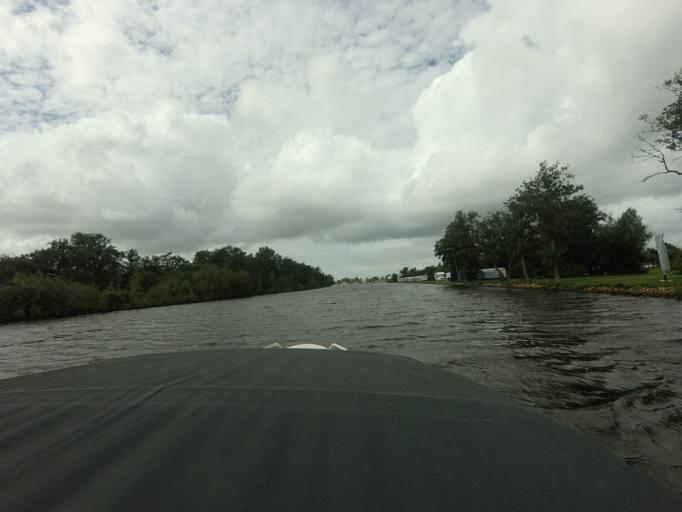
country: NL
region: Friesland
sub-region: Gemeente Boarnsterhim
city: Warten
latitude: 53.1257
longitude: 5.9382
